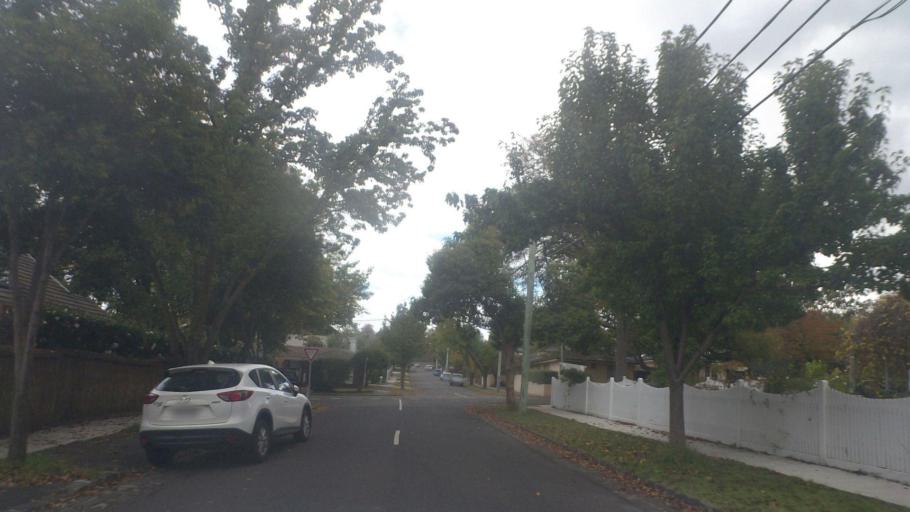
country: AU
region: Victoria
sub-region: Whitehorse
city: Surrey Hills
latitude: -37.8242
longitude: 145.1098
